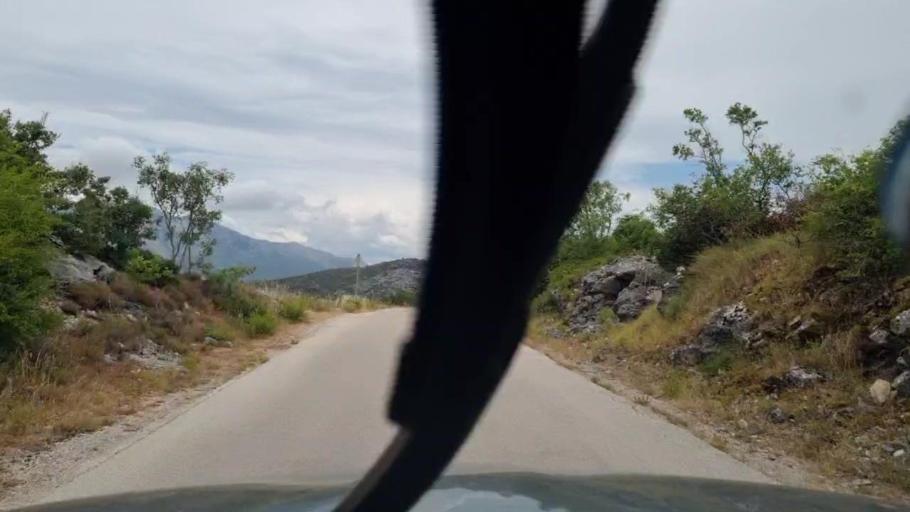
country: BA
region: Federation of Bosnia and Herzegovina
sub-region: Hercegovacko-Bosanski Kanton
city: Neum
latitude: 42.9308
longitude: 17.6886
